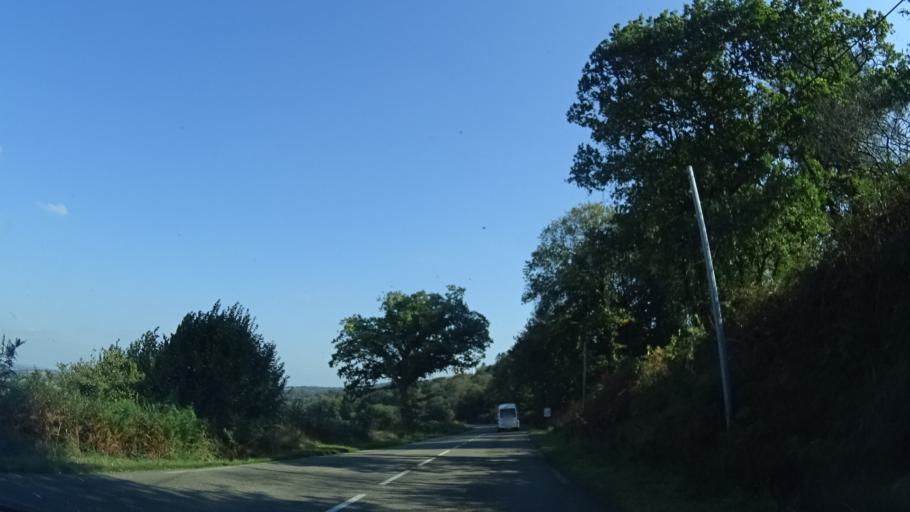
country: FR
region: Brittany
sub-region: Departement du Finistere
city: Cast
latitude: 48.1780
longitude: -4.1190
